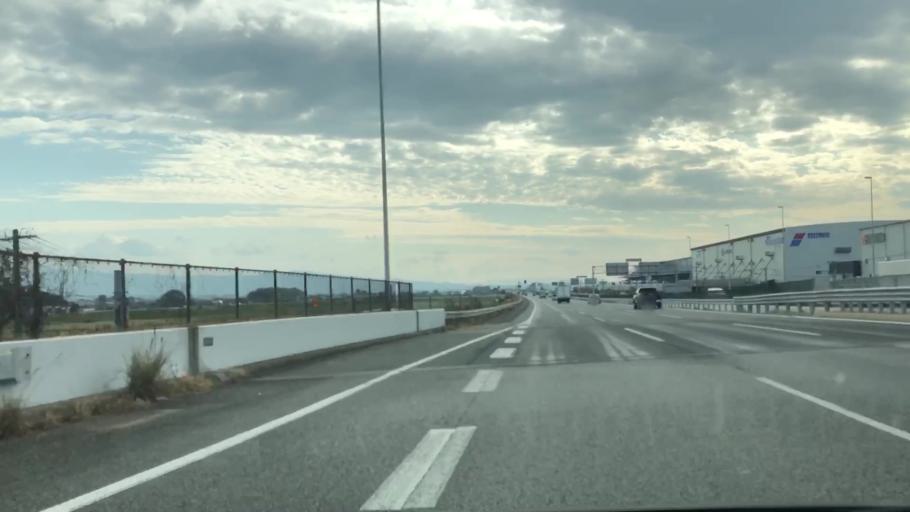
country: JP
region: Saga Prefecture
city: Tosu
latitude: 33.3922
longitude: 130.5384
